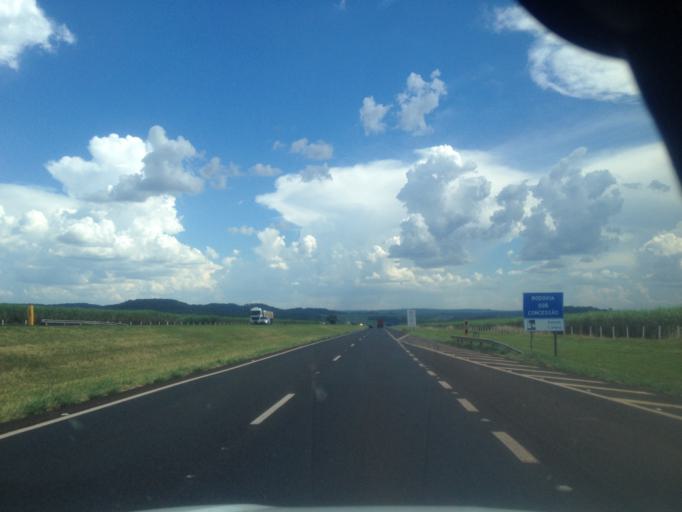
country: BR
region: Sao Paulo
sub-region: Ituverava
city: Ituverava
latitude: -20.2024
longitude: -47.7865
